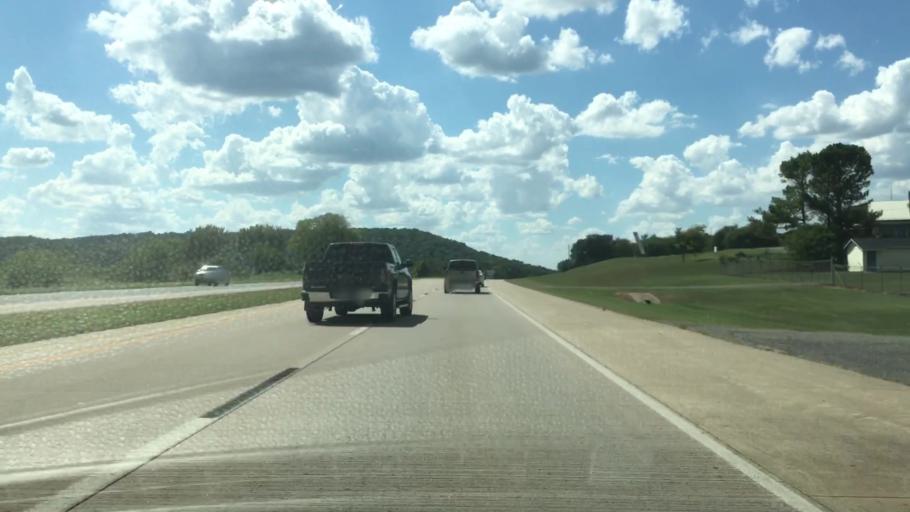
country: US
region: Oklahoma
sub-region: Cherokee County
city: Park Hill
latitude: 35.8029
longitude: -95.0868
